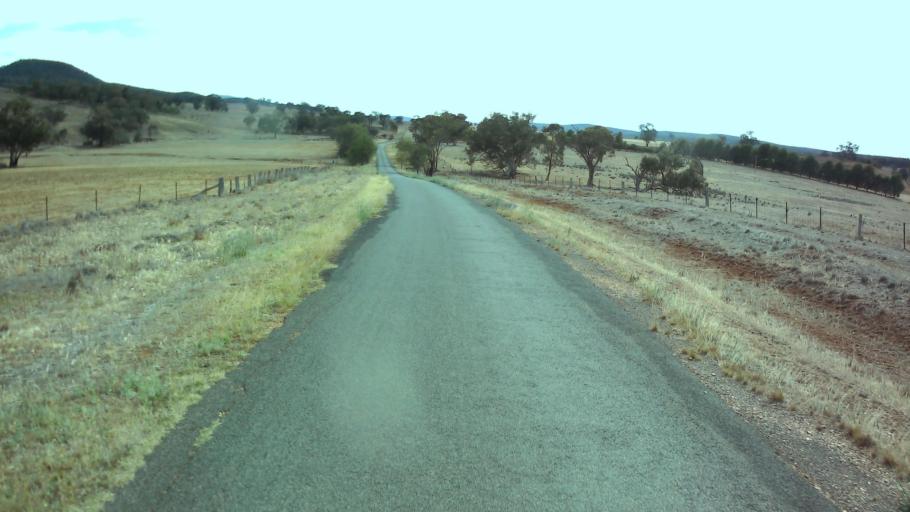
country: AU
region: New South Wales
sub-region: Weddin
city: Grenfell
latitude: -33.8424
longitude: 148.2616
